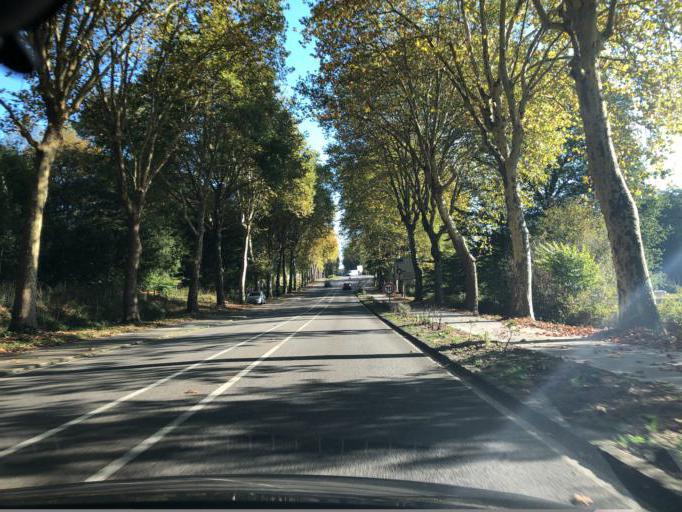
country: FR
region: Ile-de-France
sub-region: Departement des Yvelines
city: Rambouillet
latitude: 48.6607
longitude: 1.8288
